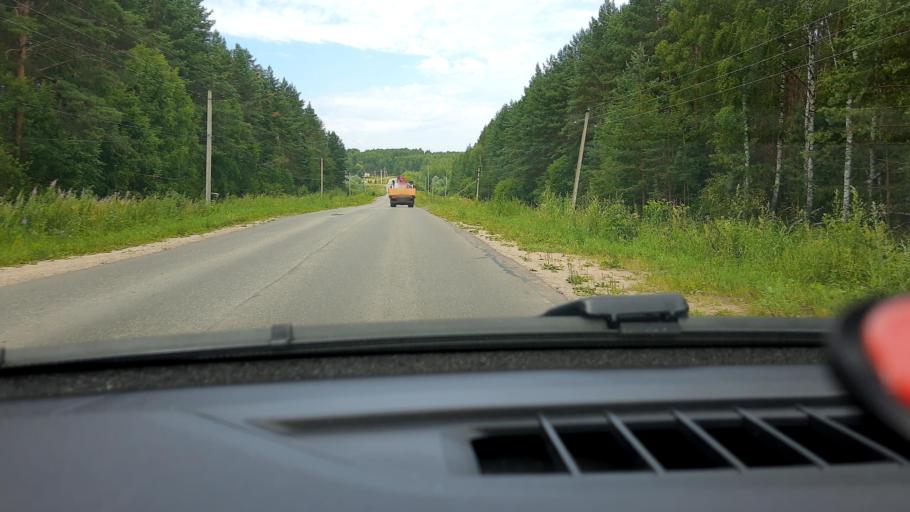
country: RU
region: Nizjnij Novgorod
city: Bogorodsk
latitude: 56.1351
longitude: 43.5909
